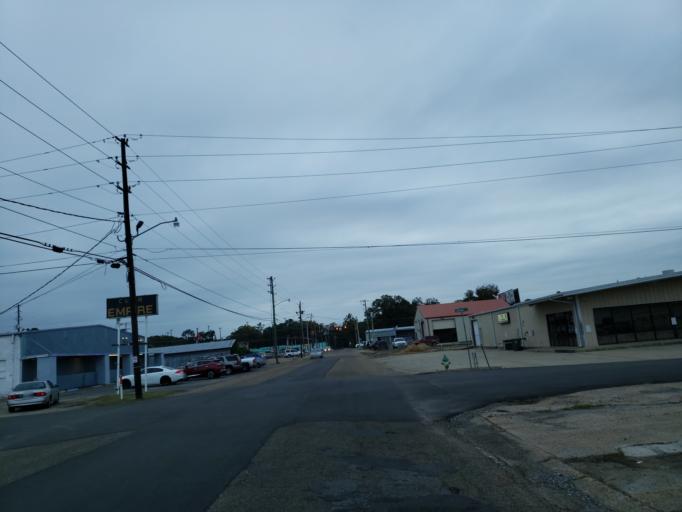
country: US
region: Mississippi
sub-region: Forrest County
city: Hattiesburg
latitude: 31.3129
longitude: -89.3080
